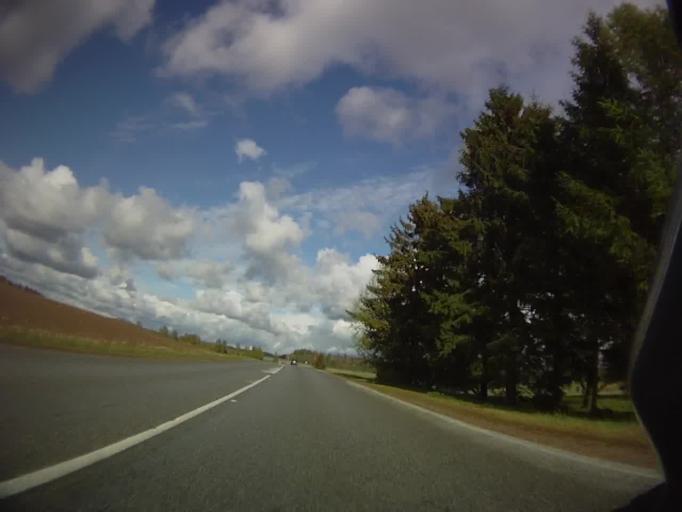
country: LV
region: Sigulda
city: Sigulda
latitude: 57.1640
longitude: 24.7980
